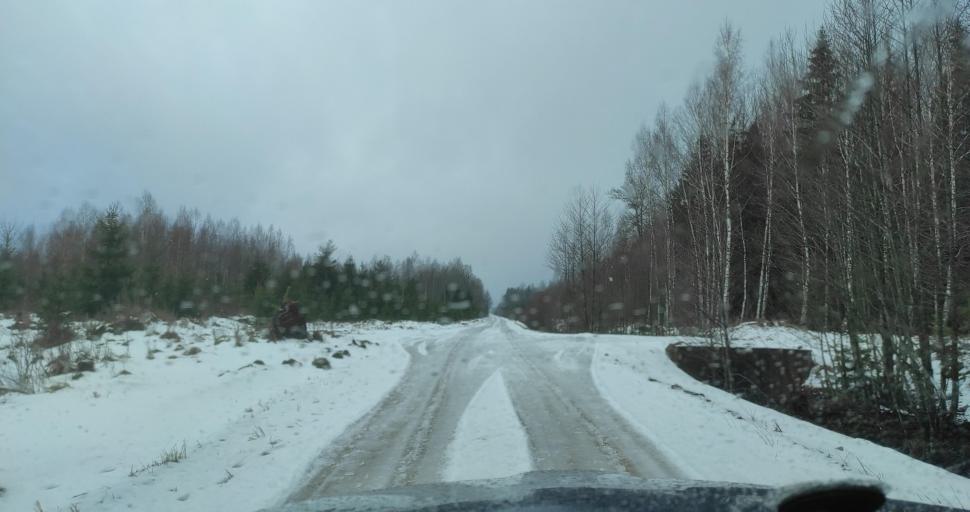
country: LV
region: Dundaga
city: Dundaga
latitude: 57.3870
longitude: 22.1407
